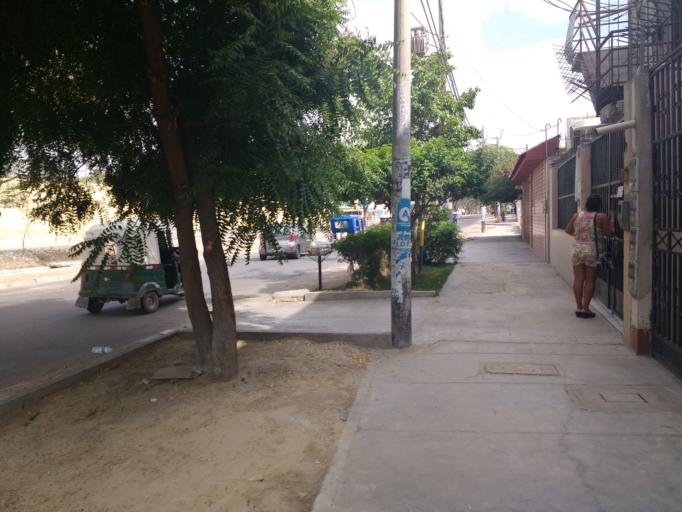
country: PE
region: Piura
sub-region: Provincia de Piura
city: Piura
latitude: -5.1886
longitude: -80.6487
